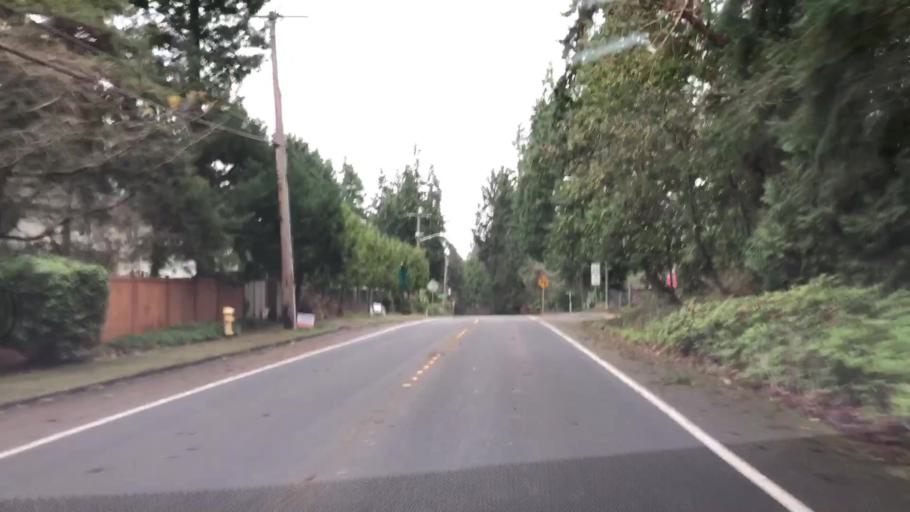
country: US
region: Washington
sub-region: King County
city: West Lake Sammamish
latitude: 47.5889
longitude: -122.1197
